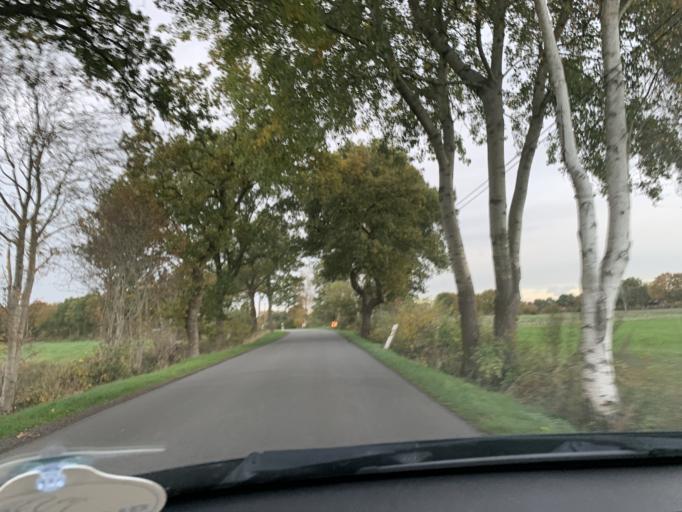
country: DE
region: Lower Saxony
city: Wiefelstede
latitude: 53.2801
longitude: 8.0278
